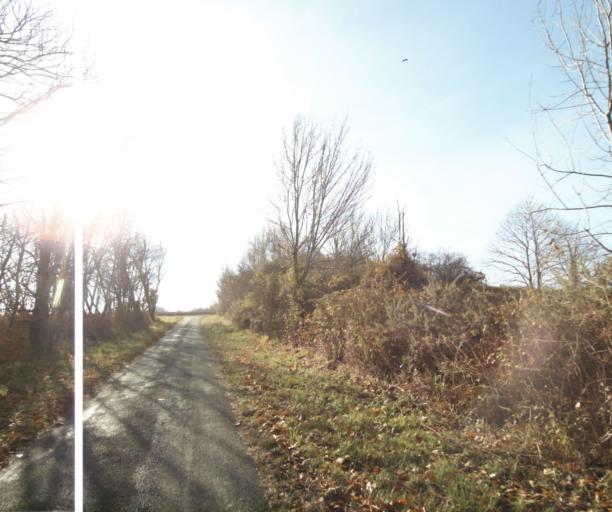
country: FR
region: Poitou-Charentes
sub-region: Departement de la Charente-Maritime
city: Burie
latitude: 45.7514
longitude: -0.4826
